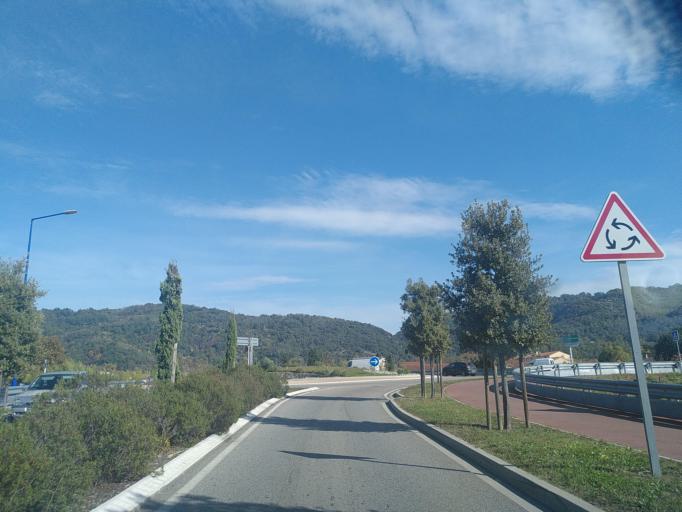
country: FR
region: Rhone-Alpes
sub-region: Departement de la Drome
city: Saint-Vallier
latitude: 45.1728
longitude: 4.8135
